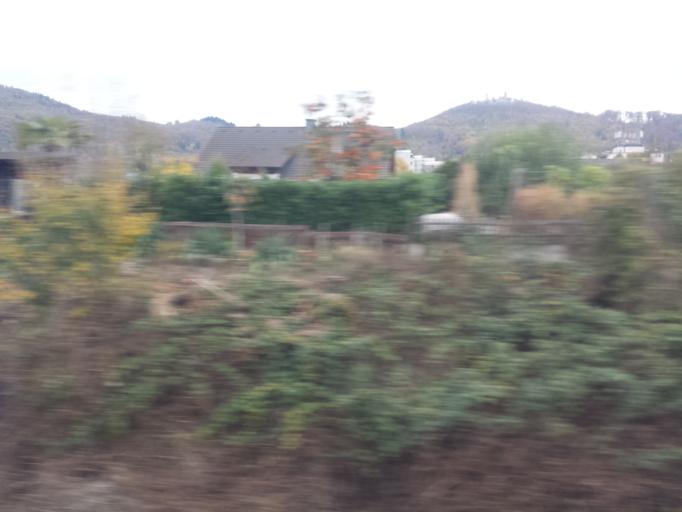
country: DE
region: Hesse
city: Zwingenberg
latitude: 49.7086
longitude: 8.6120
